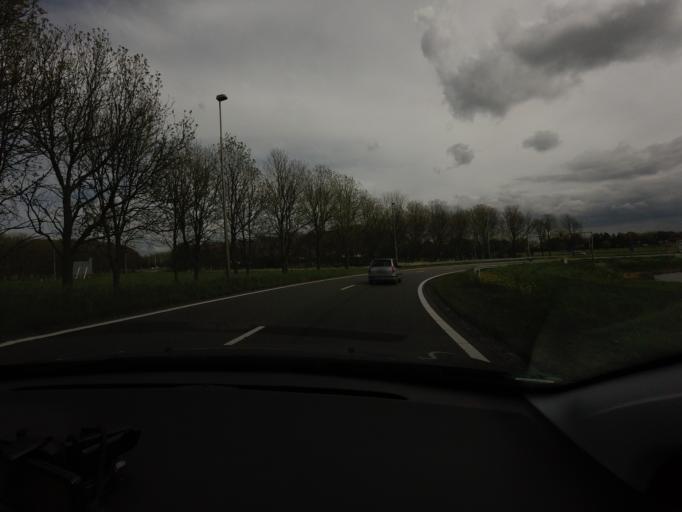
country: NL
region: North Holland
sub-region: Gemeente Beemster
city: Halfweg
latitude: 52.5335
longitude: 4.9467
